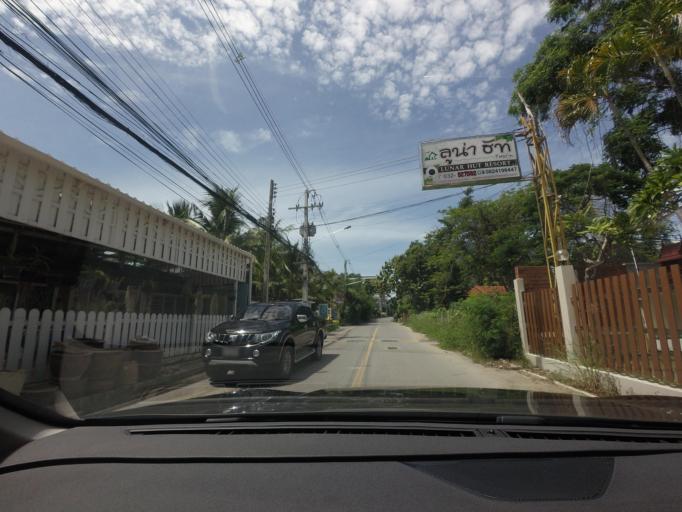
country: TH
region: Prachuap Khiri Khan
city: Hua Hin
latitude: 12.5125
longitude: 99.9758
